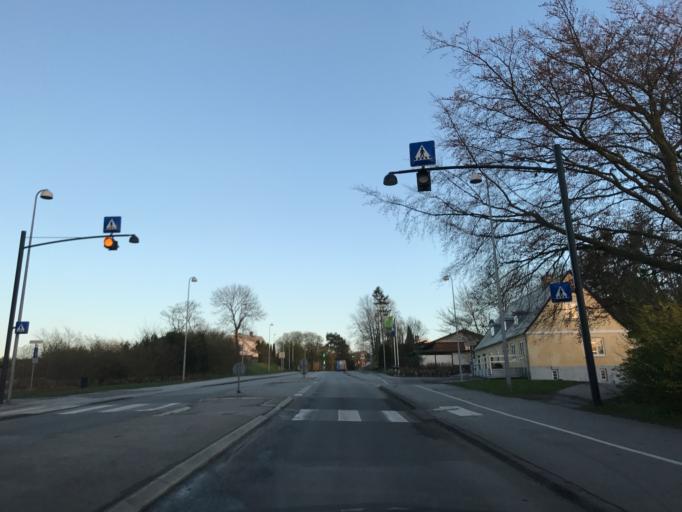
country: DK
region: Capital Region
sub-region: Horsholm Kommune
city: Horsholm
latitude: 55.8932
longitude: 12.4938
